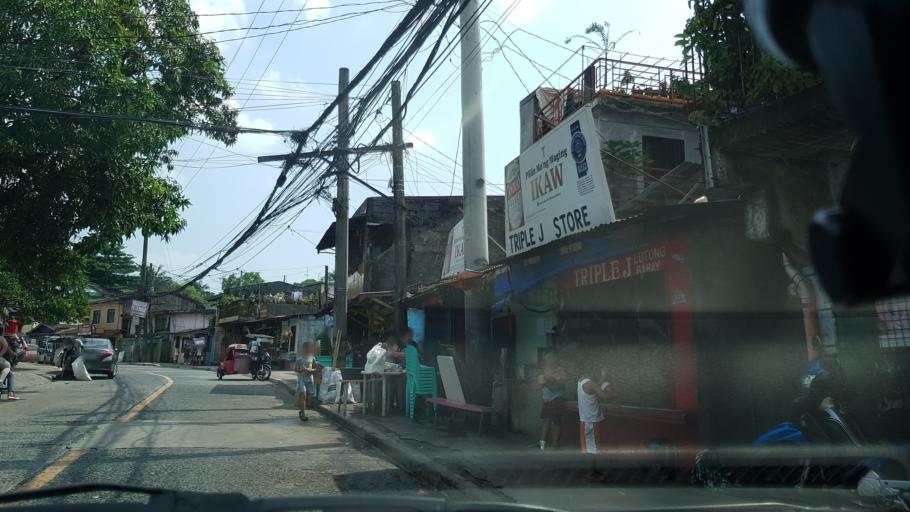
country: PH
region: Calabarzon
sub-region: Province of Rizal
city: Antipolo
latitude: 14.6596
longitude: 121.1282
